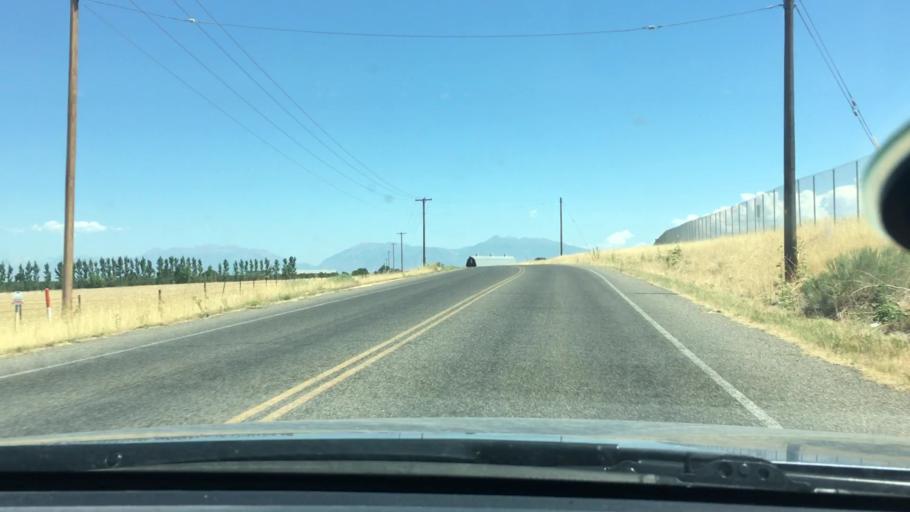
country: US
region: Utah
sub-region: Utah County
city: Santaquin
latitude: 39.9568
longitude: -111.7979
